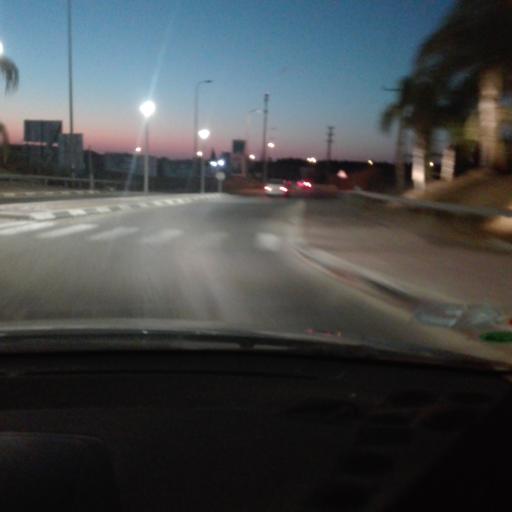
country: PS
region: West Bank
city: Nazlat `Isa
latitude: 32.4296
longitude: 35.0308
